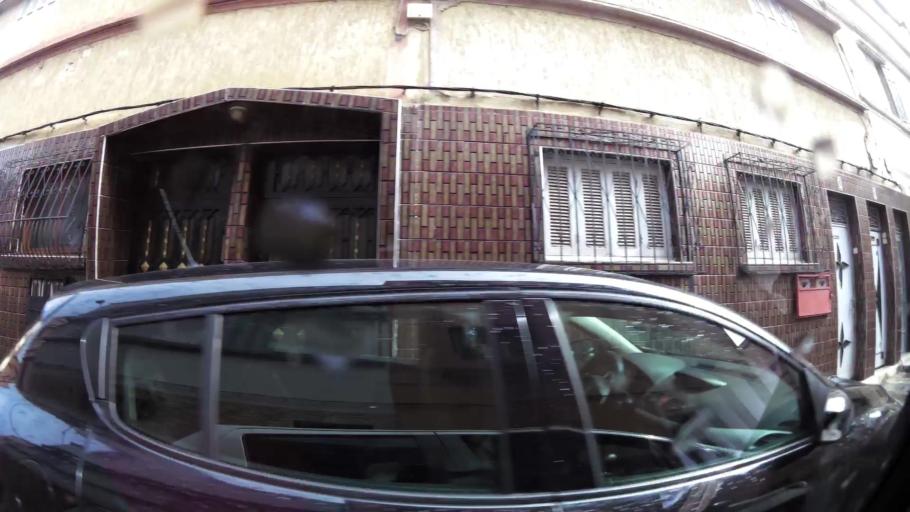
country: MA
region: Grand Casablanca
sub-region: Casablanca
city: Casablanca
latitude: 33.5456
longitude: -7.5724
